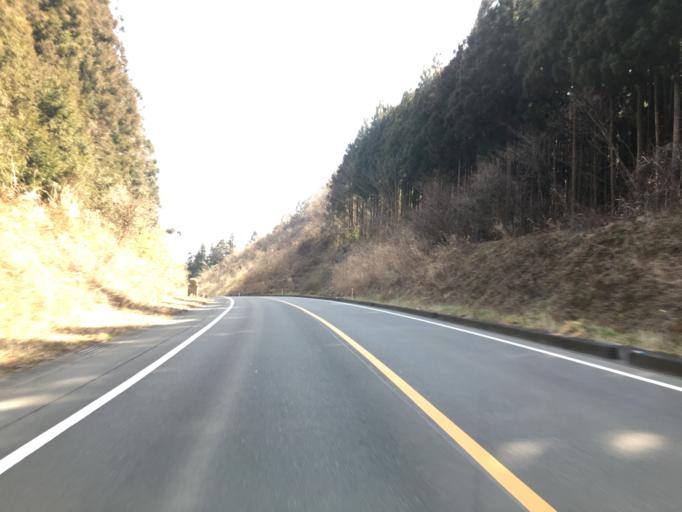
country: JP
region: Ibaraki
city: Daigo
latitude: 36.7976
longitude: 140.4734
